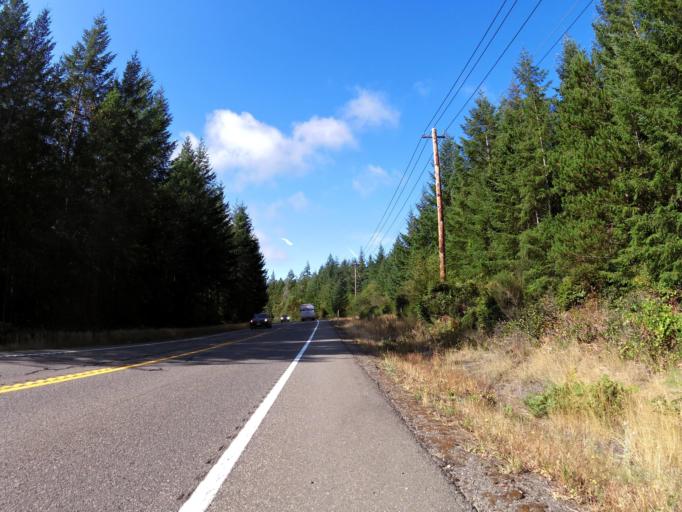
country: US
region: Washington
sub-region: Mason County
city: Allyn
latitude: 47.3208
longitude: -122.9050
